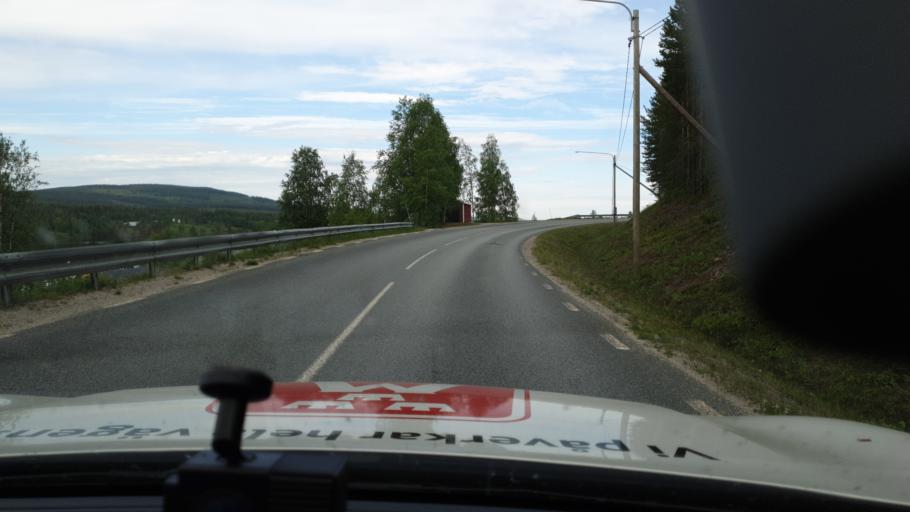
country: SE
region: Vaesterbotten
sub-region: Lycksele Kommun
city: Soderfors
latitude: 65.0947
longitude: 18.3186
